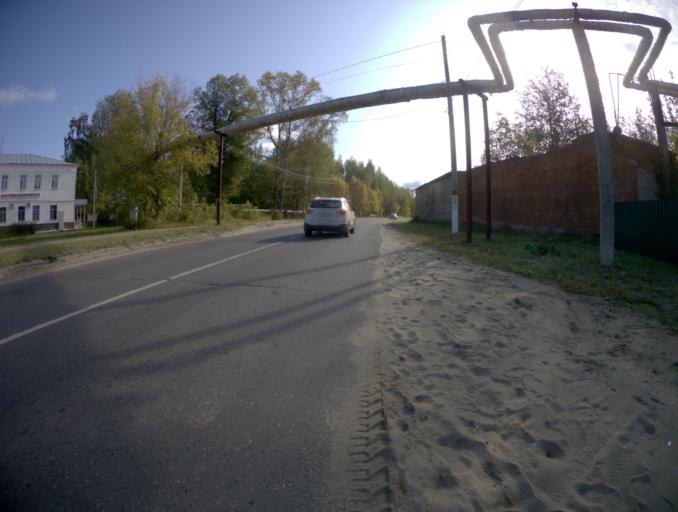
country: RU
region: Moskovskaya
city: Roshal'
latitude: 55.6624
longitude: 39.8698
